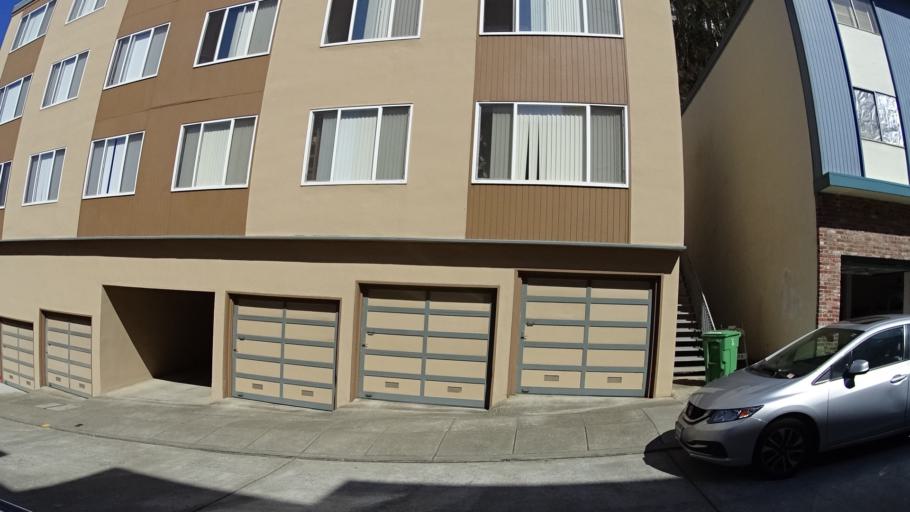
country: US
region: California
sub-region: San Francisco County
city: San Francisco
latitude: 37.7579
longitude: -122.4621
